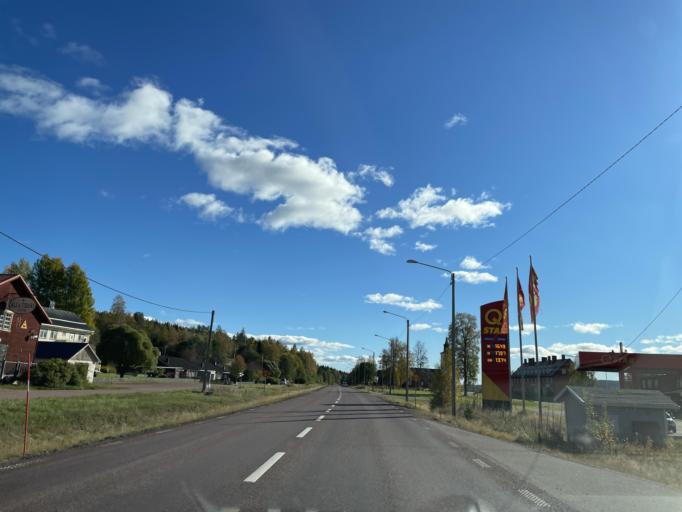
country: SE
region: Dalarna
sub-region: Malung-Saelens kommun
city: Malung
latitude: 60.9364
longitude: 13.3606
